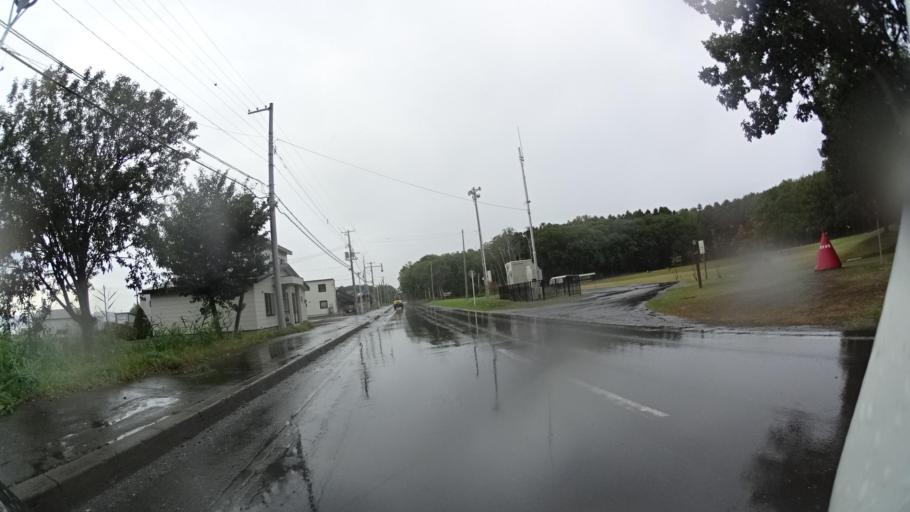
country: JP
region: Hokkaido
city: Mombetsu
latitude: 44.3236
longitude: 143.5027
